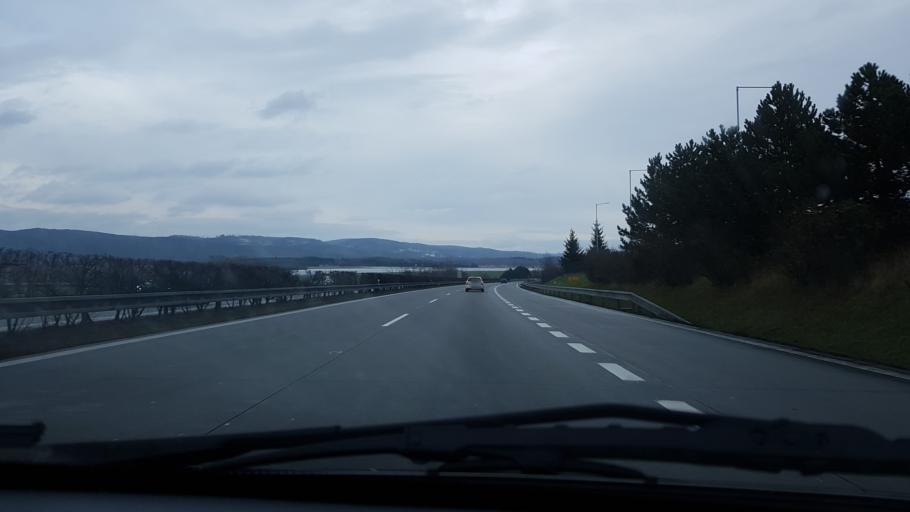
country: CZ
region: Olomoucky
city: Doloplazy
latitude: 49.5854
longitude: 17.4144
